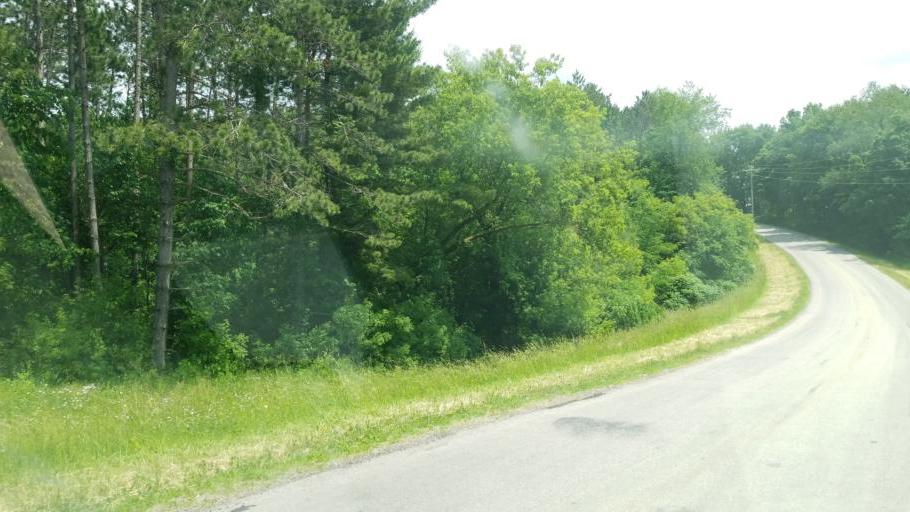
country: US
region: Wisconsin
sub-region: Monroe County
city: Cashton
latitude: 43.6980
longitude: -90.6508
